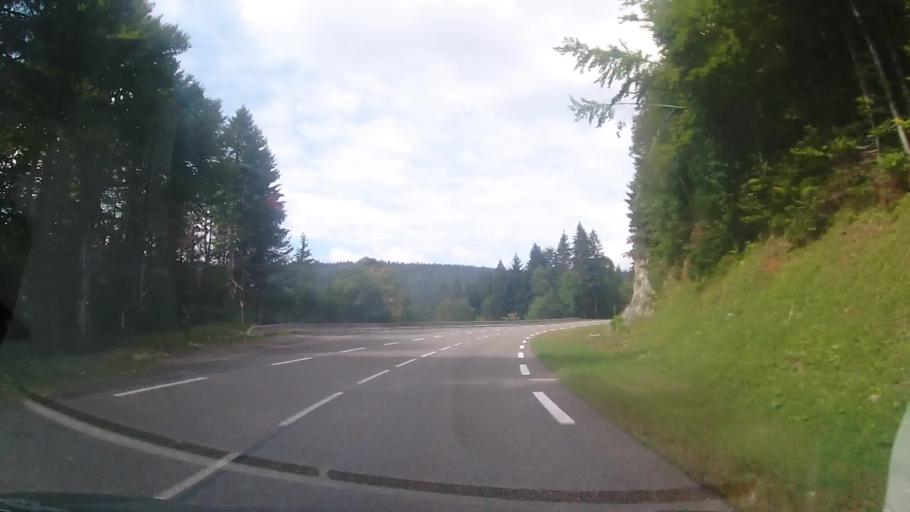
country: FR
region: Rhone-Alpes
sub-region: Departement de l'Ain
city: Gex
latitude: 46.4079
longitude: 6.0571
